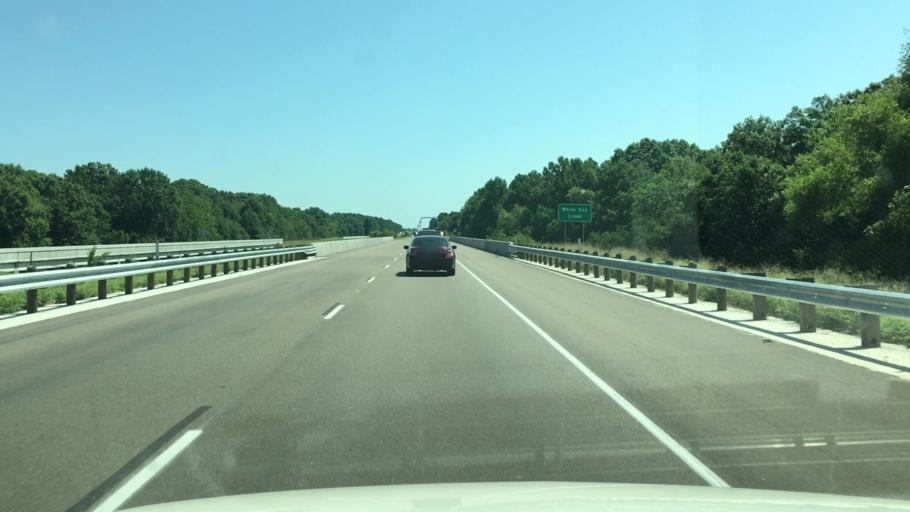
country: US
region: Texas
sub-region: Morris County
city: Omaha
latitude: 33.2748
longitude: -94.8074
